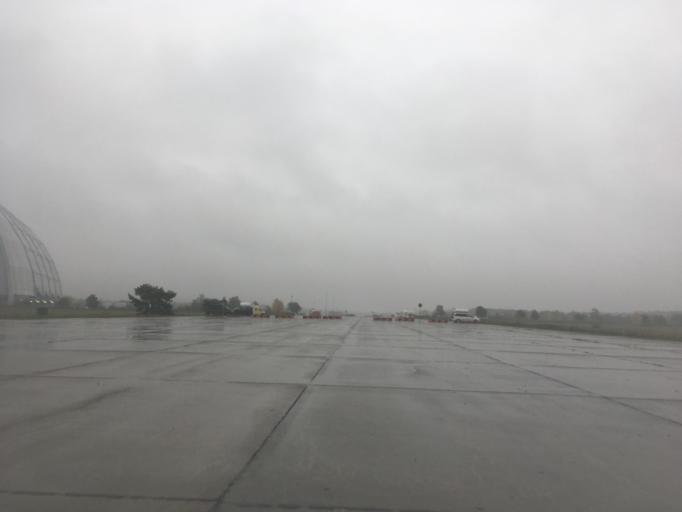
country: DE
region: Brandenburg
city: Halbe
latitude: 52.0361
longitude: 13.7414
